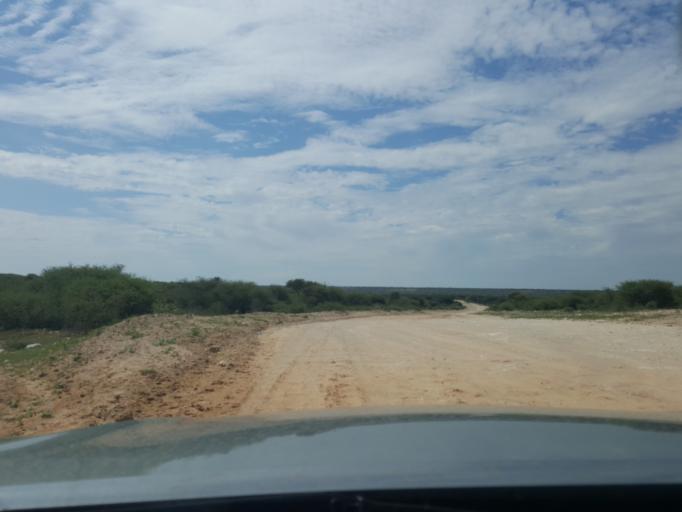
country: BW
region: Kweneng
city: Letlhakeng
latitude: -24.0707
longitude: 25.0295
